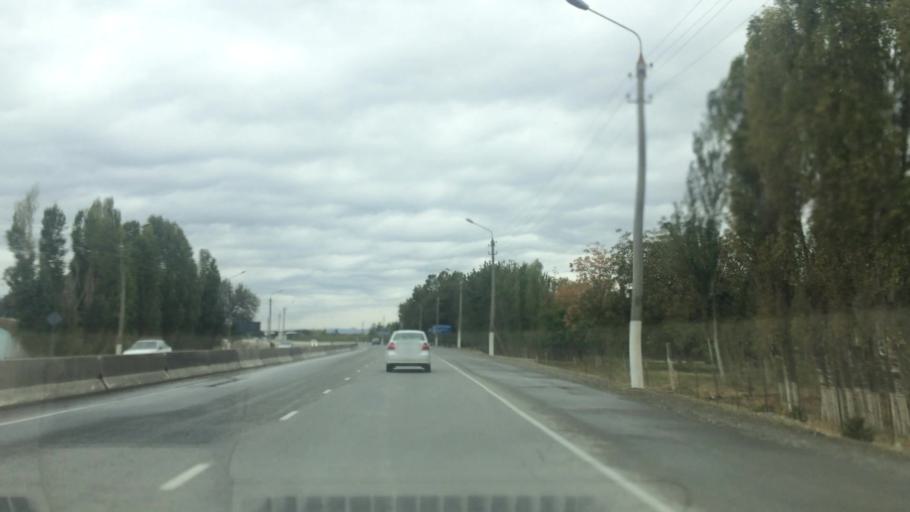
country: UZ
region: Jizzax
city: Jizzax
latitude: 39.9786
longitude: 67.5654
